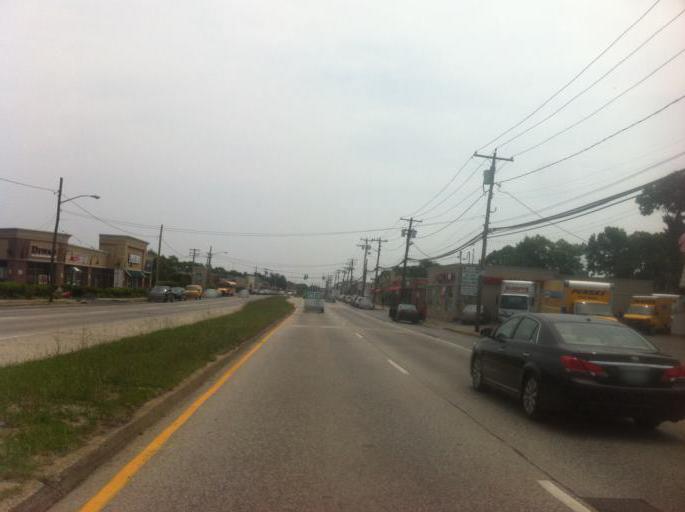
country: US
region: New York
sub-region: Nassau County
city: Hicksville
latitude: 40.7597
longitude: -73.5141
